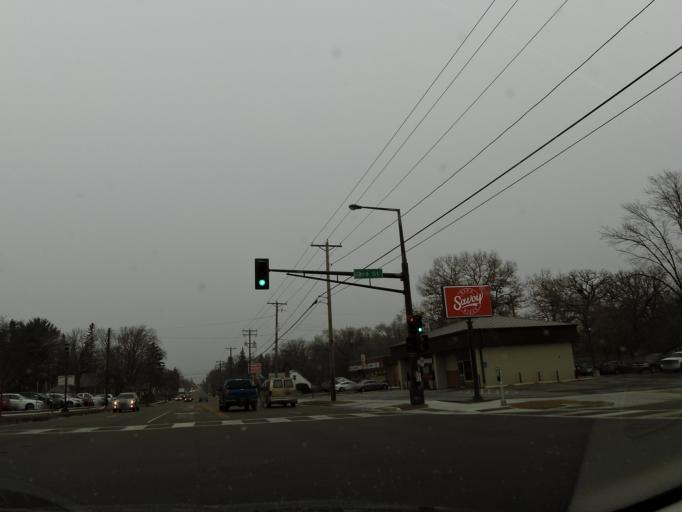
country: US
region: Minnesota
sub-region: Ramsey County
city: Maplewood
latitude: 44.9568
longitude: -93.0254
